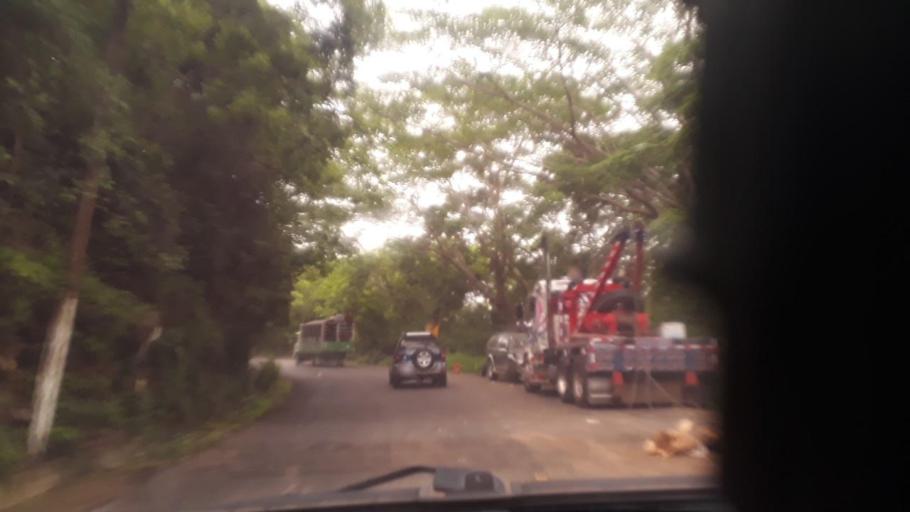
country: GT
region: Jutiapa
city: Jalpatagua
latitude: 14.1668
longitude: -90.0502
